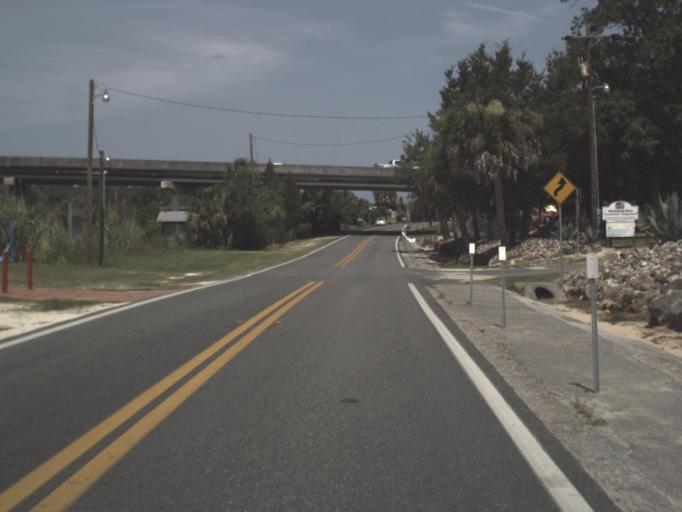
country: US
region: Florida
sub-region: Taylor County
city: Steinhatchee
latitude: 29.6684
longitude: -83.3771
